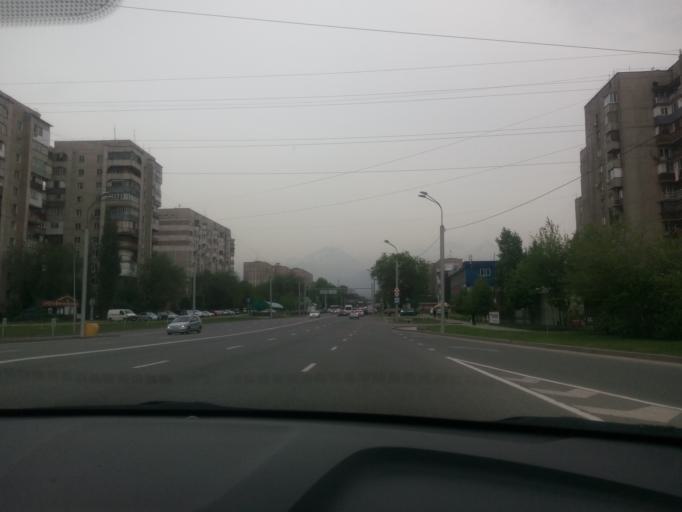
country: KZ
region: Almaty Qalasy
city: Almaty
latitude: 43.2416
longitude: 76.8284
